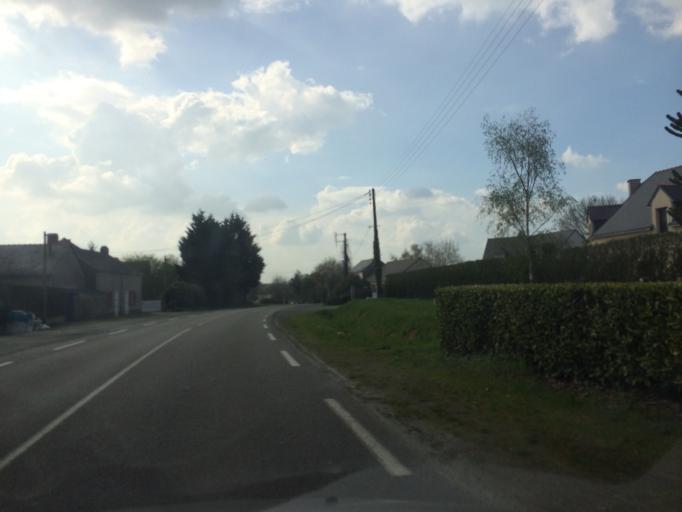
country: FR
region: Pays de la Loire
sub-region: Departement de la Loire-Atlantique
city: Blain
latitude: 47.4819
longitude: -1.7948
